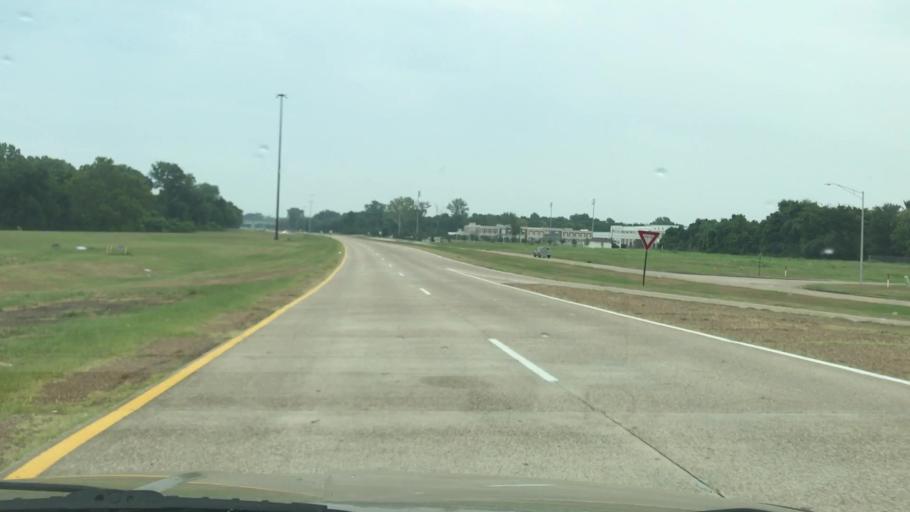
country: US
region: Louisiana
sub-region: Bossier Parish
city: Bossier City
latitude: 32.4992
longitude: -93.7144
